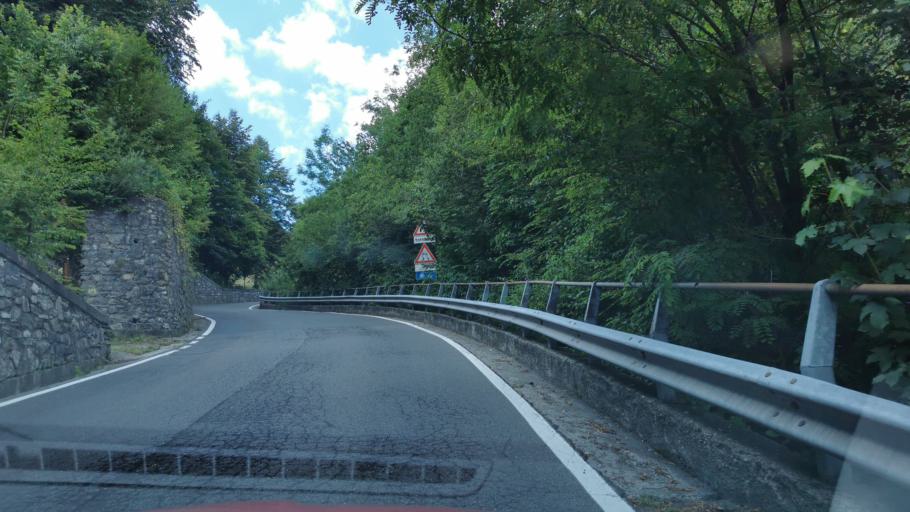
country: IT
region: Lombardy
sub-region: Provincia di Como
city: Pellio Intelvi
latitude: 45.9766
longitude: 9.0640
